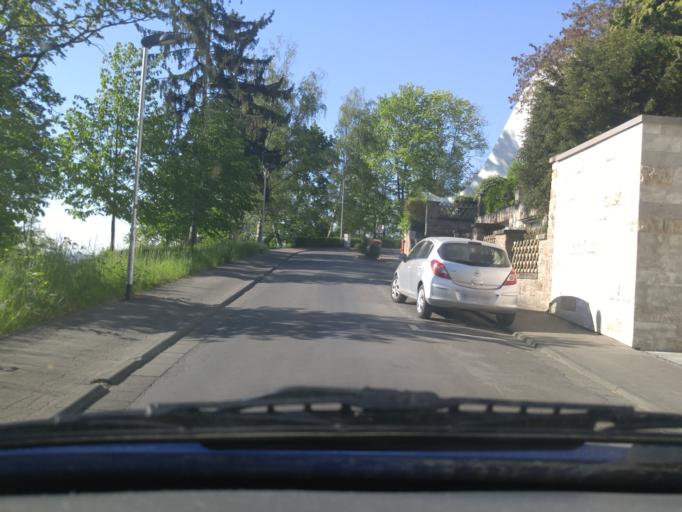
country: DE
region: Hesse
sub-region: Regierungsbezirk Darmstadt
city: Bad Nauheim
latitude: 50.3667
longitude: 8.7329
